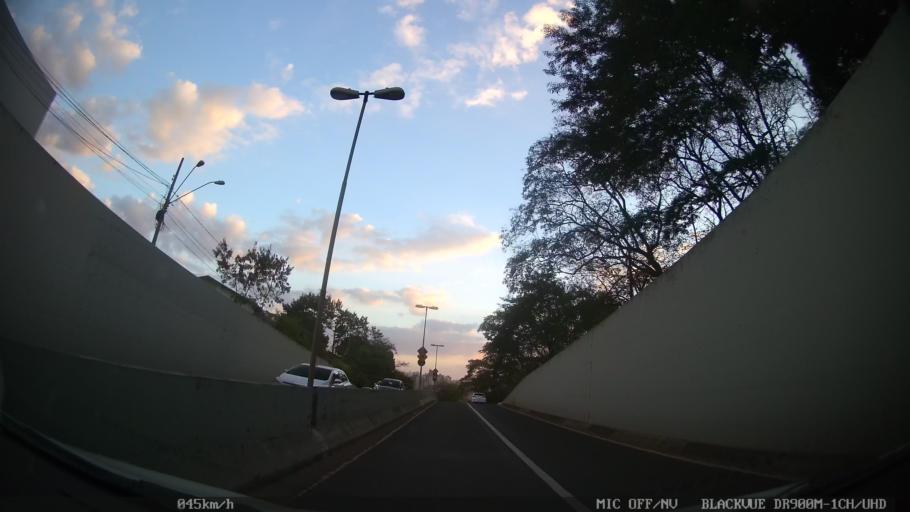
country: BR
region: Sao Paulo
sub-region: Ribeirao Preto
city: Ribeirao Preto
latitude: -21.1751
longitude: -47.7954
